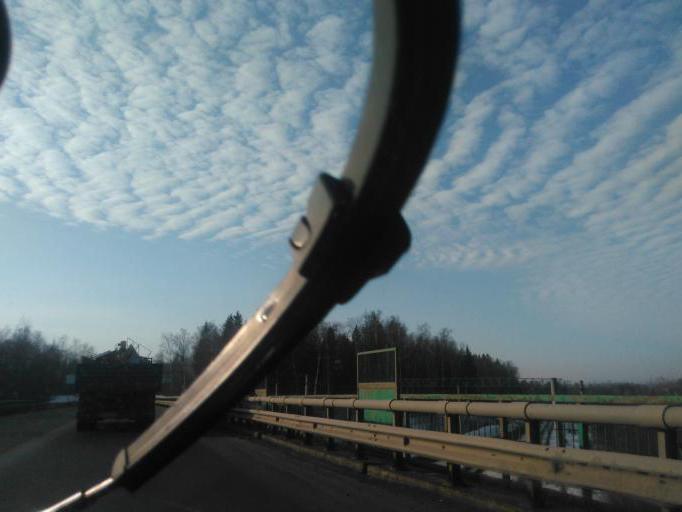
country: RU
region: Moskovskaya
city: Istra
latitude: 55.8942
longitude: 36.9443
